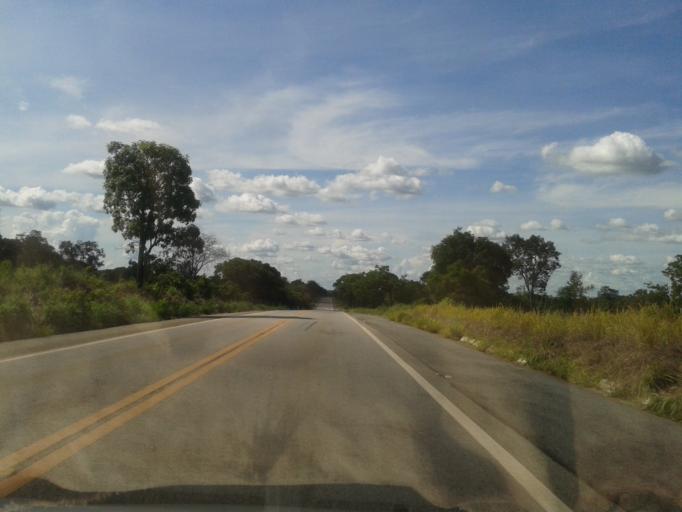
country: BR
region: Goias
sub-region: Mozarlandia
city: Mozarlandia
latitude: -15.2314
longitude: -50.5193
